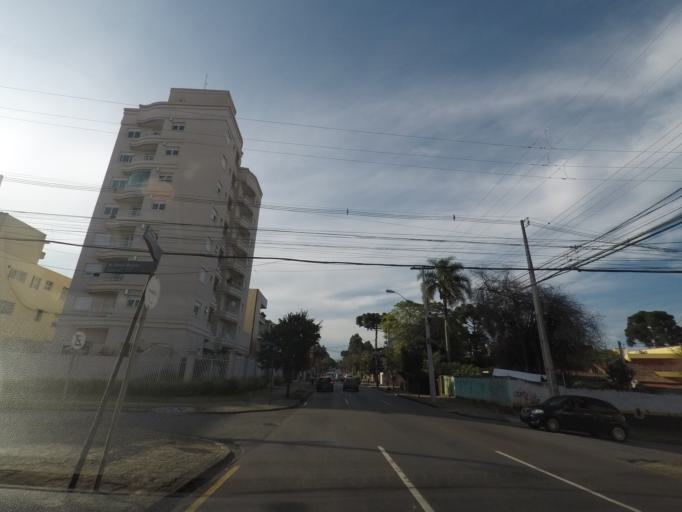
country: BR
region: Parana
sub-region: Curitiba
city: Curitiba
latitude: -25.4197
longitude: -49.2528
